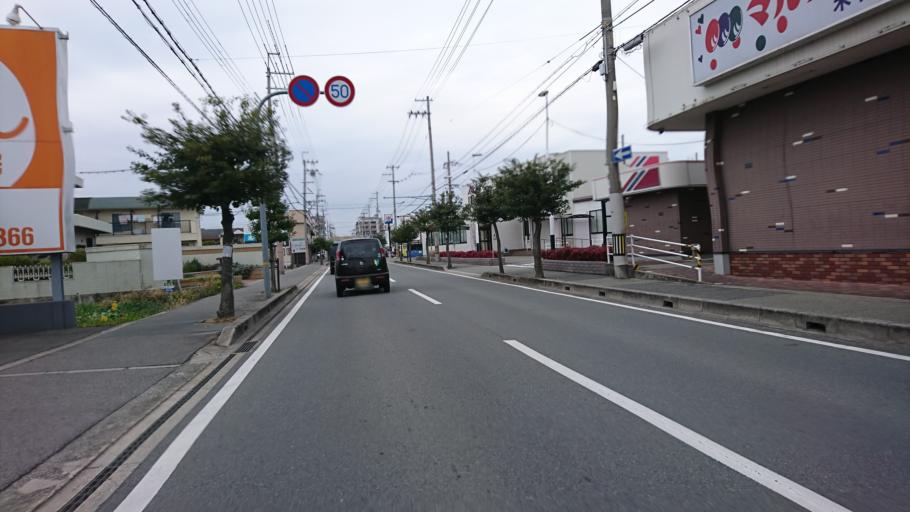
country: JP
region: Hyogo
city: Kakogawacho-honmachi
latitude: 34.7644
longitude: 134.8293
